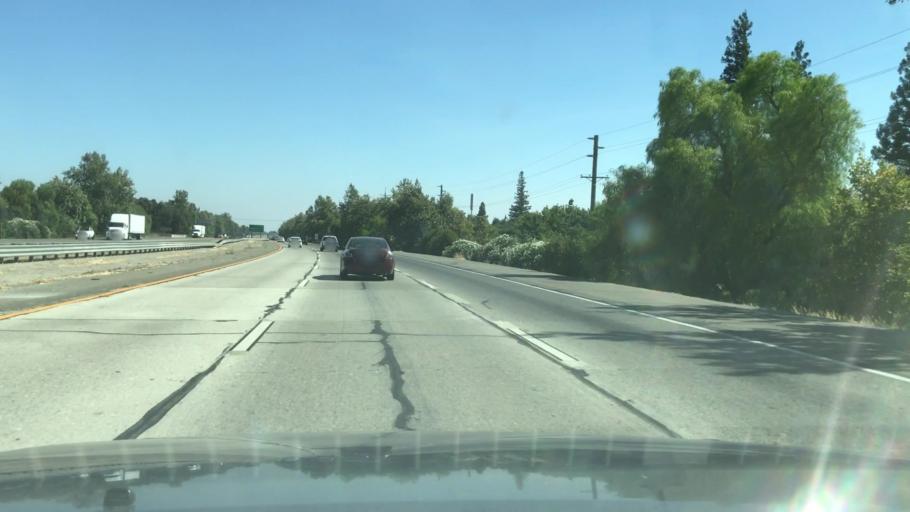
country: US
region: California
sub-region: San Joaquin County
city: Lincoln Village
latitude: 38.0348
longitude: -121.3657
